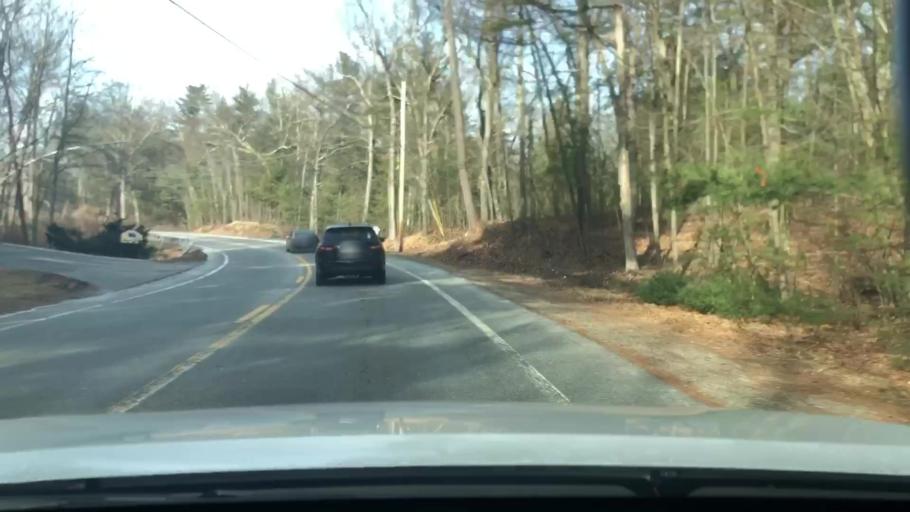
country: US
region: Massachusetts
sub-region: Worcester County
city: Grafton
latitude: 42.1990
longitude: -71.6569
